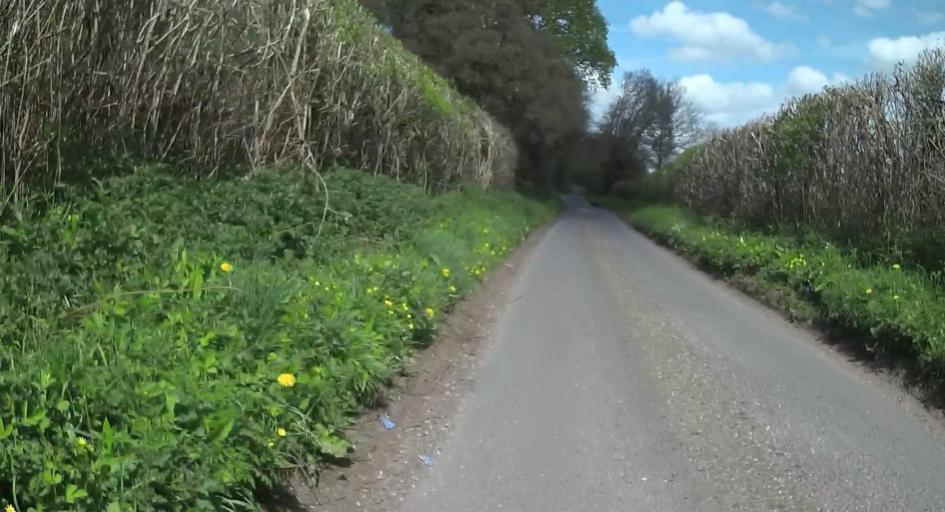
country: GB
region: England
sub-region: Hampshire
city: Romsey
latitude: 51.0511
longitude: -1.5357
